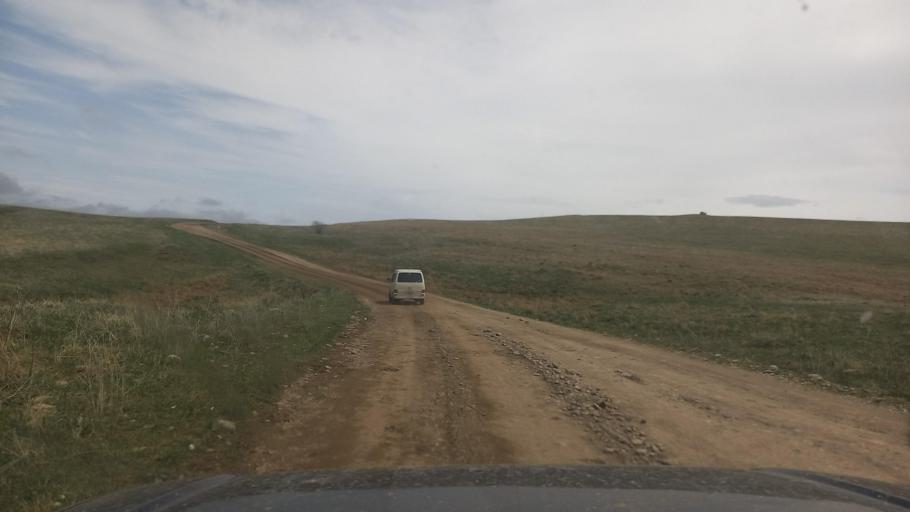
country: RU
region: Stavropol'skiy
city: Kislovodsk
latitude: 43.7662
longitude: 42.8244
